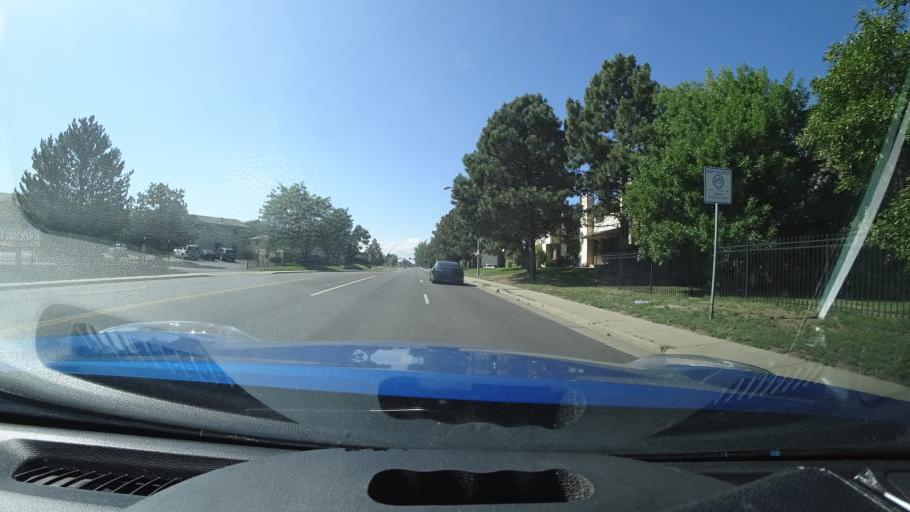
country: US
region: Colorado
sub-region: Adams County
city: Aurora
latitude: 39.6963
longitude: -104.8193
